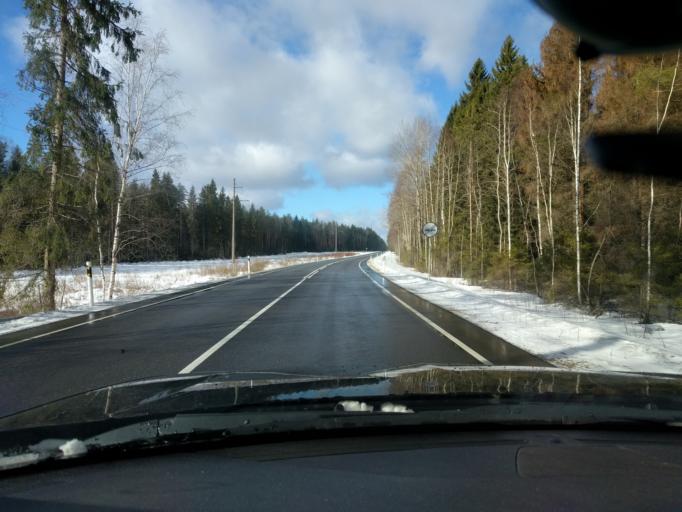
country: EE
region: Harju
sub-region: Kuusalu vald
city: Kuusalu
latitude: 59.2063
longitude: 25.5673
